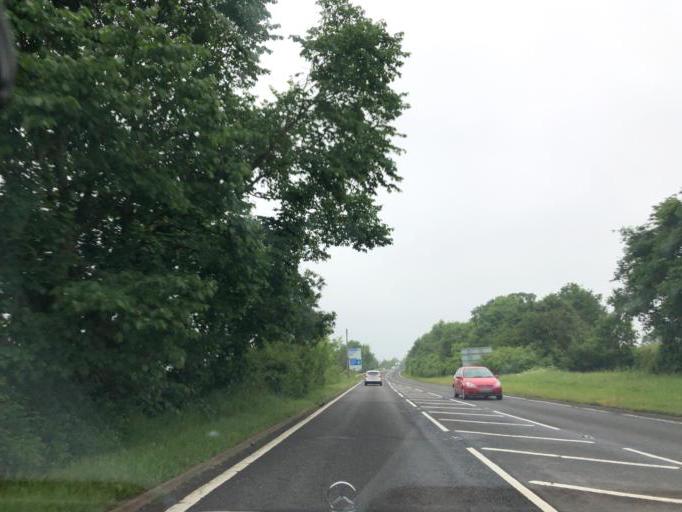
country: GB
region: England
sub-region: Warwickshire
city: Warwick
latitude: 52.2378
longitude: -1.5530
